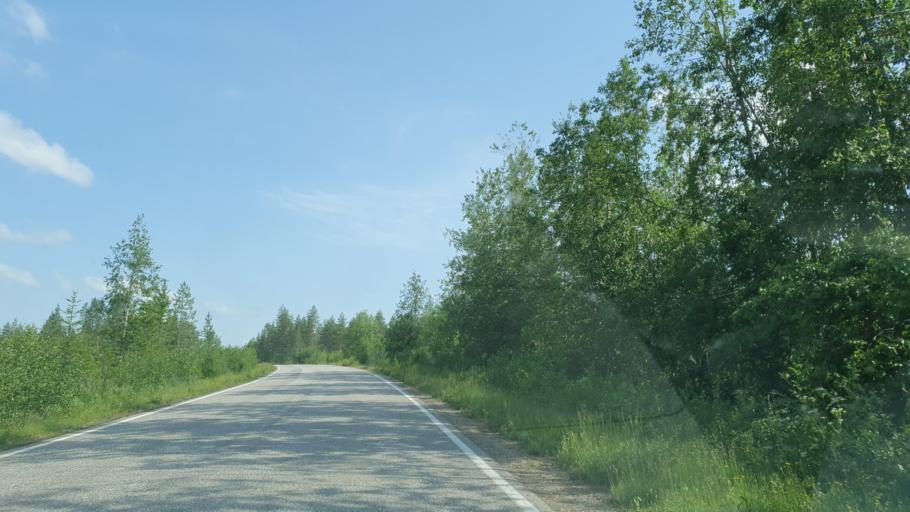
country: FI
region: Kainuu
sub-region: Kehys-Kainuu
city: Kuhmo
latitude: 64.1159
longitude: 29.7130
